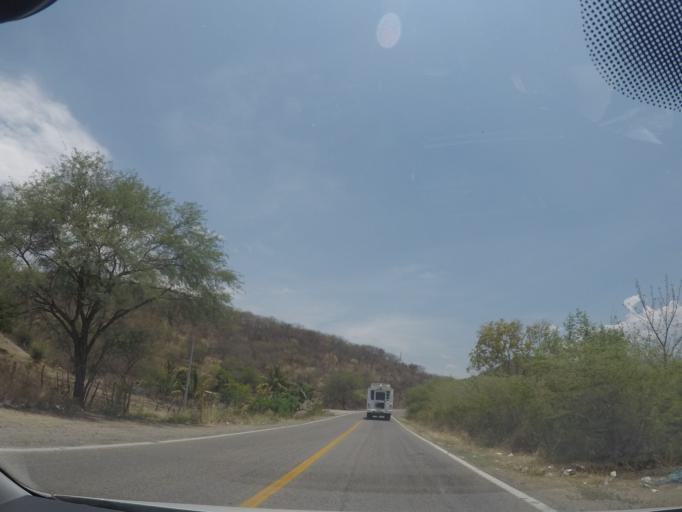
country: MX
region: Oaxaca
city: Magdalena Tequisistlan
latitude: 16.4072
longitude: -95.5897
